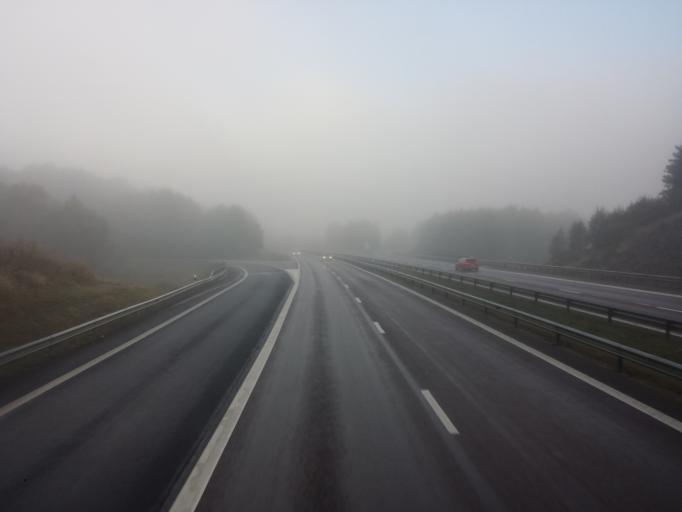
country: SE
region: Halland
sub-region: Kungsbacka Kommun
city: Fjaeras kyrkby
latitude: 57.4296
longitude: 12.1582
